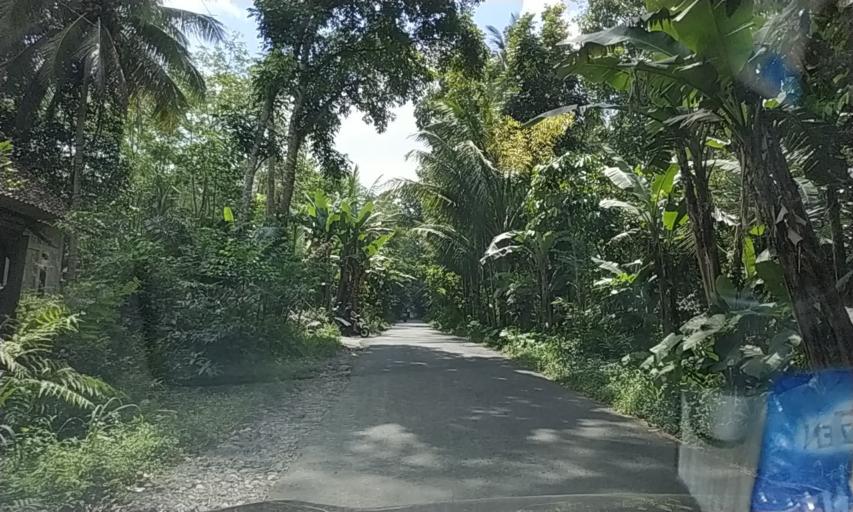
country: ID
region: Central Java
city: Jogonalan
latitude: -7.6418
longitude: 110.4695
